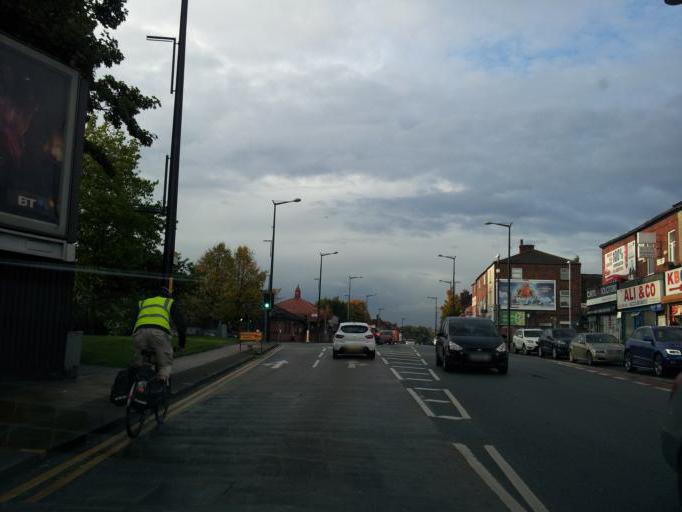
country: GB
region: England
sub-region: Manchester
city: Crumpsall
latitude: 53.5096
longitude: -2.2432
